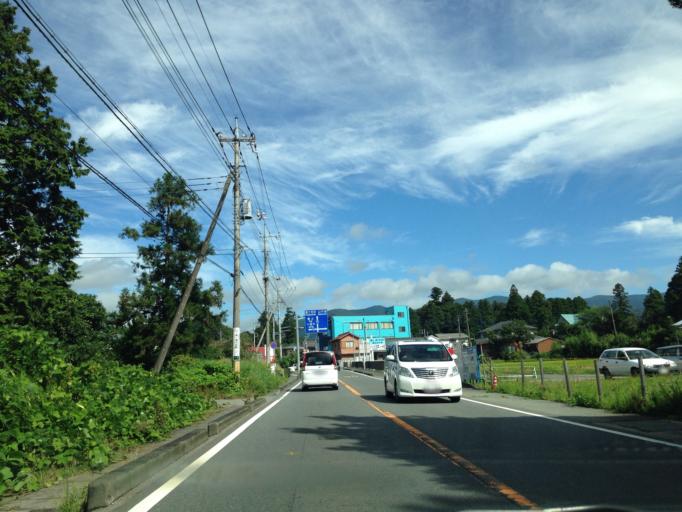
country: JP
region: Shizuoka
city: Gotemba
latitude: 35.3222
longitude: 138.9109
